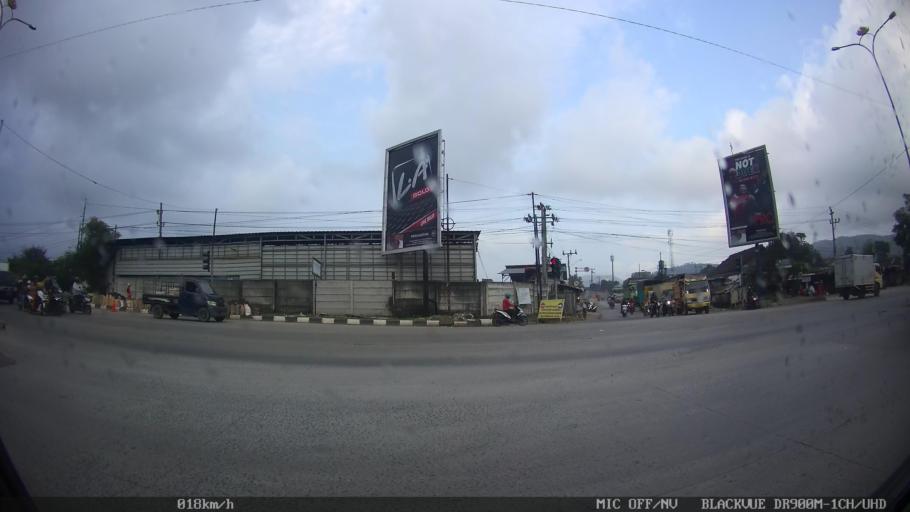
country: ID
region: Lampung
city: Bandarlampung
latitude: -5.4077
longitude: 105.2935
